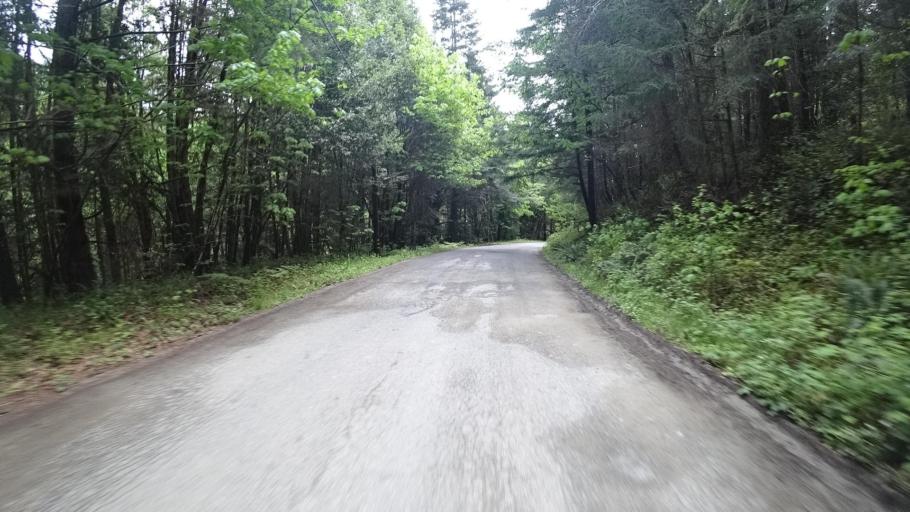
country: US
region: California
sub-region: Humboldt County
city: Blue Lake
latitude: 40.7825
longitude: -123.8792
